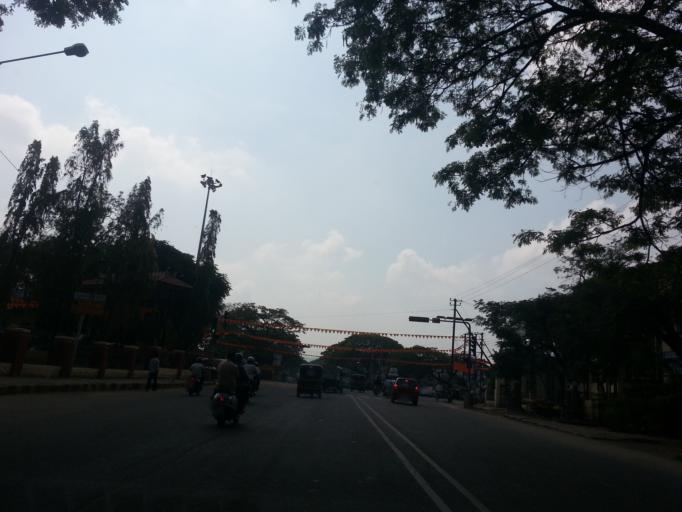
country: IN
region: Karnataka
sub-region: Mysore
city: Mysore
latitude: 12.3204
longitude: 76.6474
